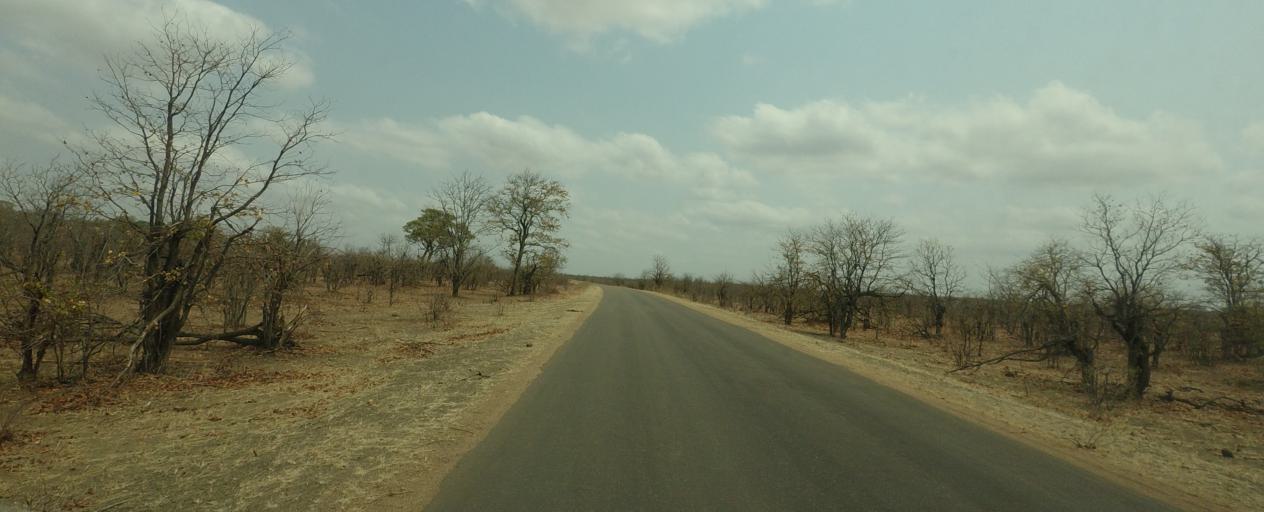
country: ZA
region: Limpopo
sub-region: Mopani District Municipality
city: Phalaborwa
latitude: -23.5541
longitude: 31.4445
